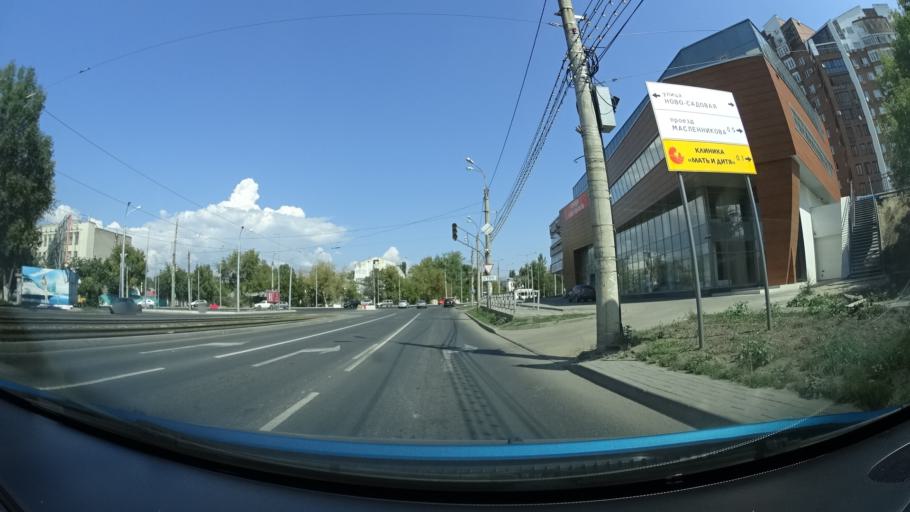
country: RU
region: Samara
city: Samara
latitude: 53.2135
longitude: 50.1440
